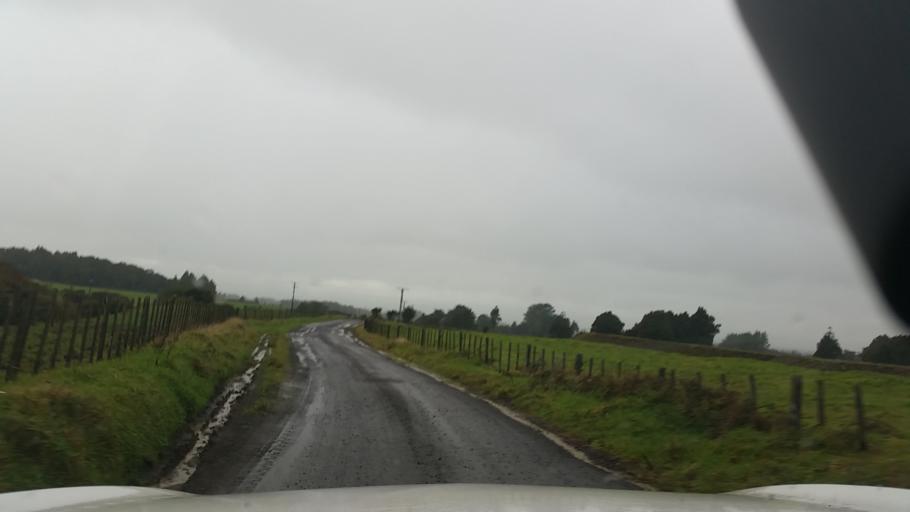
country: NZ
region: Taranaki
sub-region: South Taranaki District
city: Eltham
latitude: -39.2794
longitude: 174.1804
